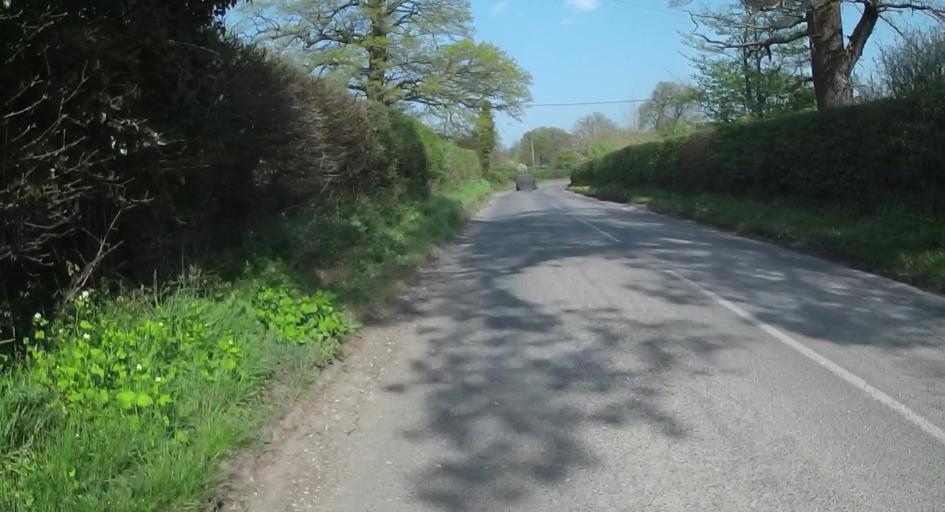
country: GB
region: England
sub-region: Hampshire
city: Basingstoke
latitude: 51.2998
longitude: -1.0975
